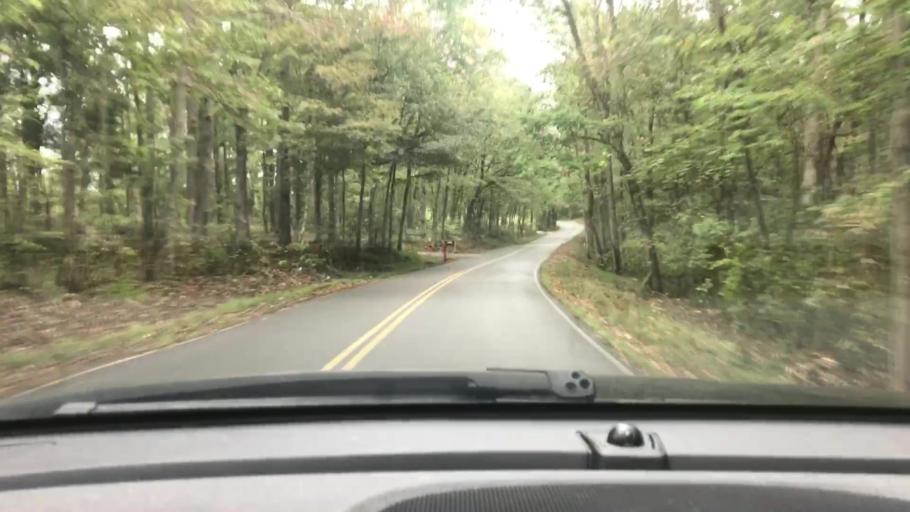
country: US
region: Tennessee
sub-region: Dickson County
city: Charlotte
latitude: 36.1909
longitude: -87.2881
